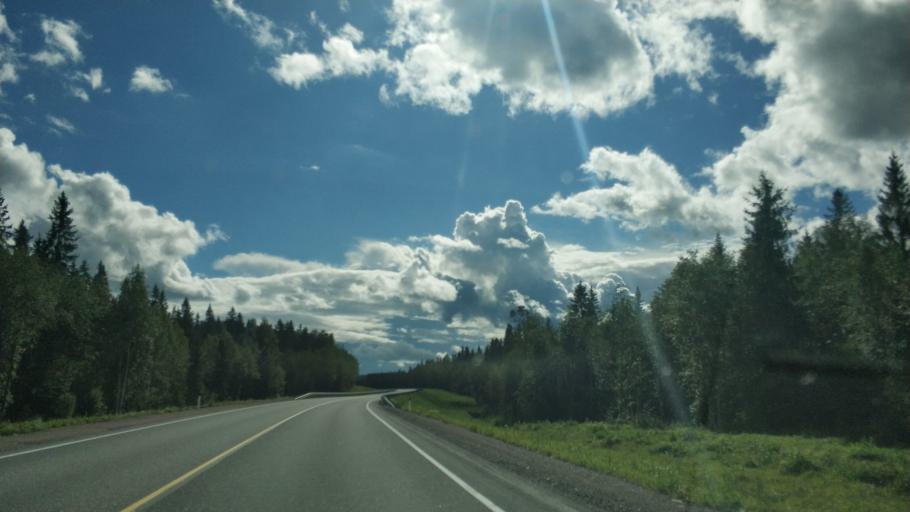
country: RU
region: Republic of Karelia
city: Ruskeala
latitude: 61.8648
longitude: 30.6537
